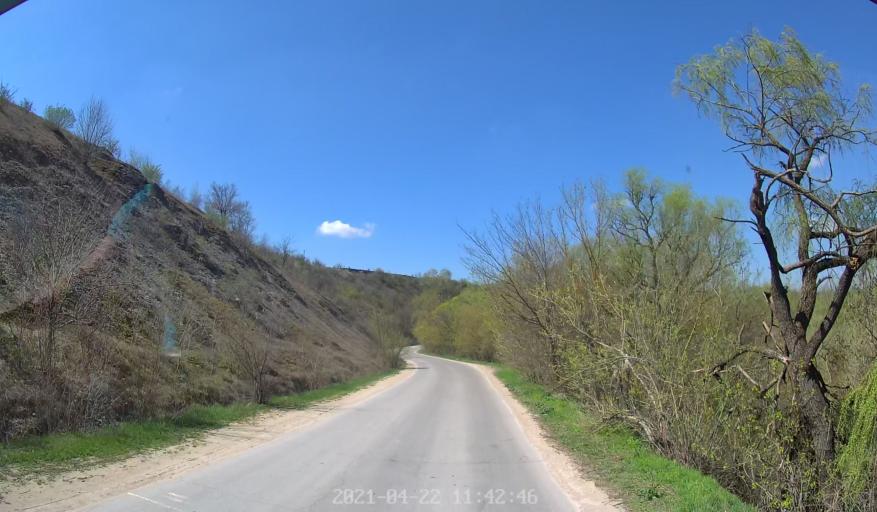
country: MD
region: Chisinau
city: Ciorescu
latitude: 47.1370
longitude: 28.9056
